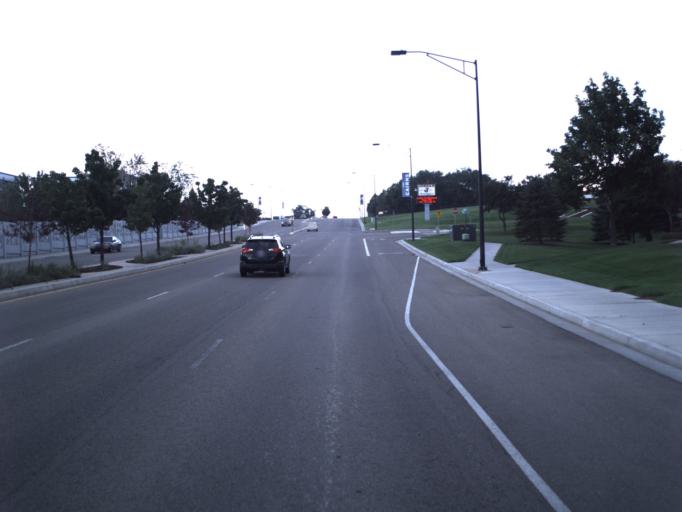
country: US
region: Utah
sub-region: Salt Lake County
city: Sandy City
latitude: 40.5716
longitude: -111.8907
